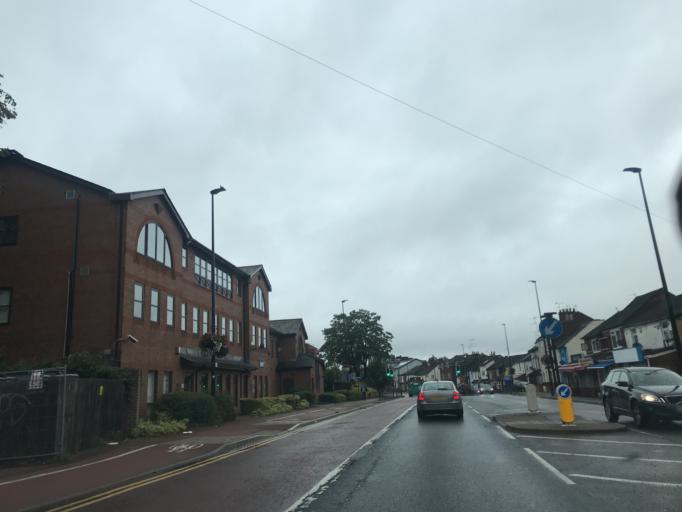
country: GB
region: England
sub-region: Buckinghamshire
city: Aylesbury
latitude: 51.8190
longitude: -0.8125
